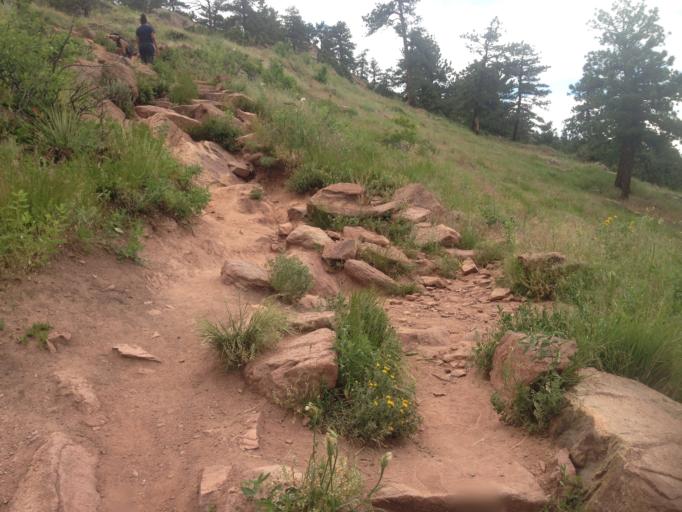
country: US
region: Colorado
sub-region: Boulder County
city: Boulder
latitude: 40.0283
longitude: -105.3018
